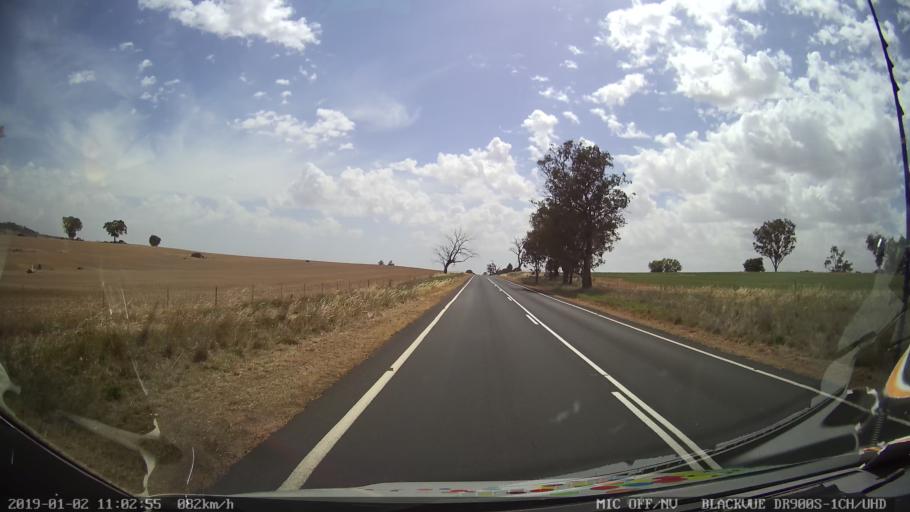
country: AU
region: New South Wales
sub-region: Young
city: Young
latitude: -34.5815
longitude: 148.3316
